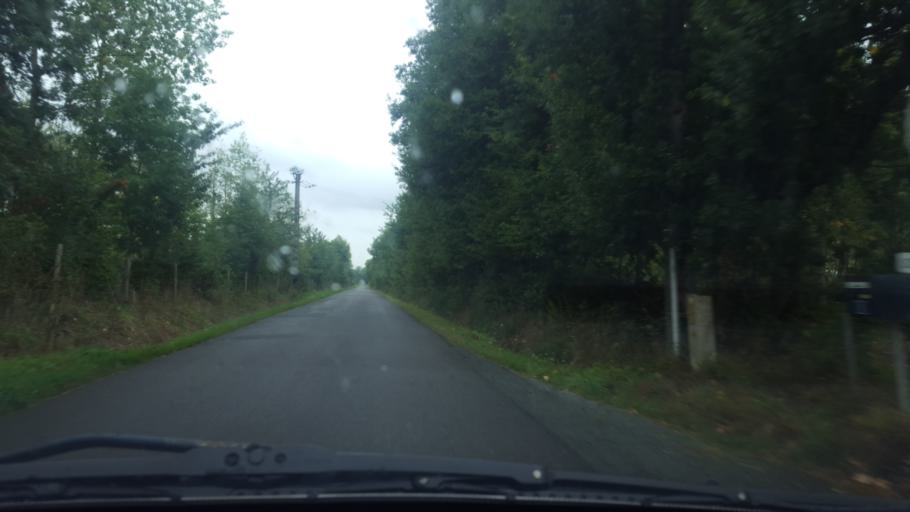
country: FR
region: Pays de la Loire
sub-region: Departement de la Loire-Atlantique
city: Saint-Philbert-de-Grand-Lieu
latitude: 47.0406
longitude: -1.6603
